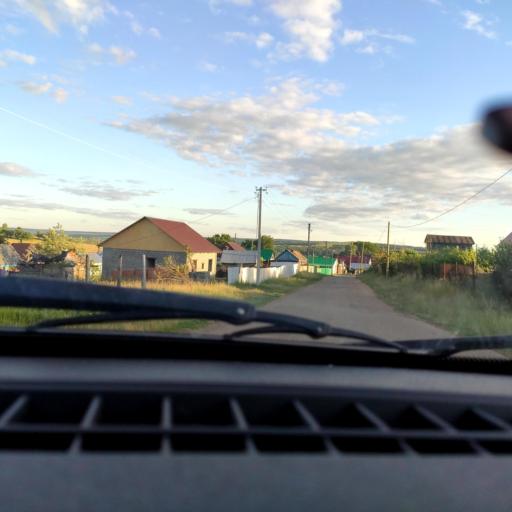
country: RU
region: Bashkortostan
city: Avdon
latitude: 54.6381
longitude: 55.5916
